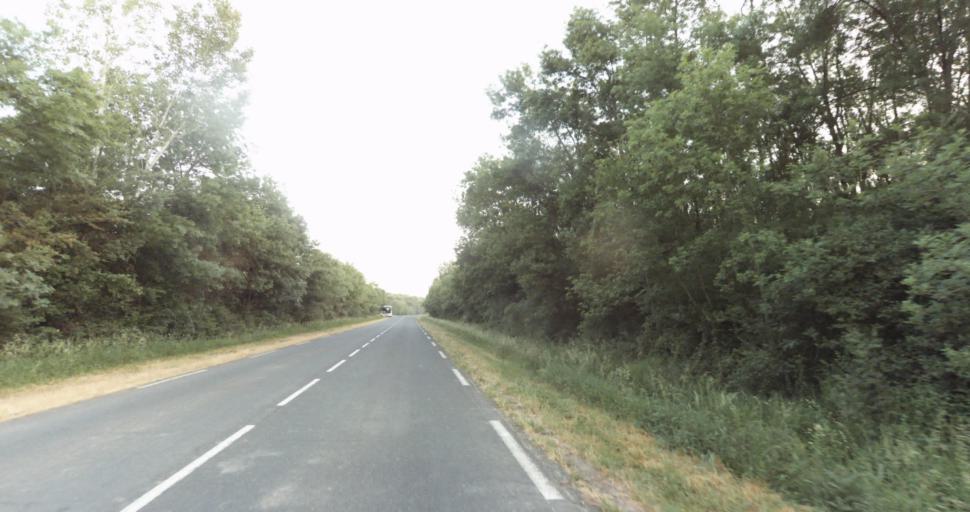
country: FR
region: Midi-Pyrenees
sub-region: Departement du Gers
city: Pujaudran
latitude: 43.6412
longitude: 1.1423
